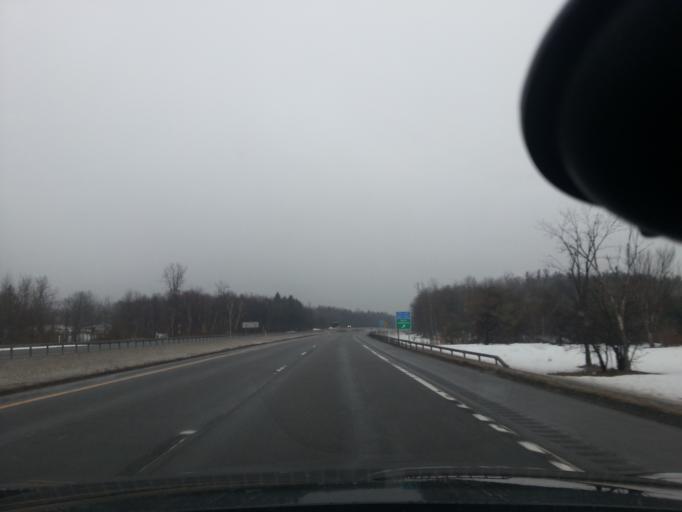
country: US
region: New York
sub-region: Jefferson County
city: Adams Center
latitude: 43.9058
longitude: -75.9809
